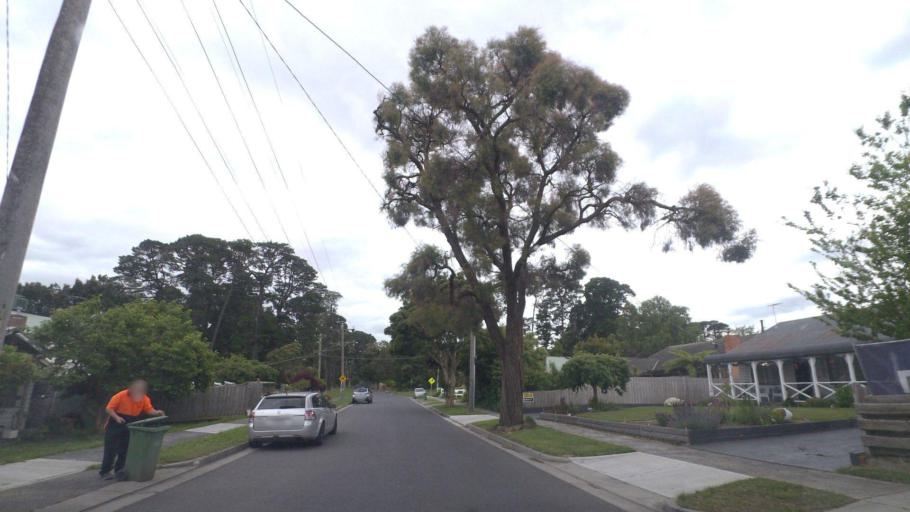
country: AU
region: Victoria
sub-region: Yarra Ranges
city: Mount Evelyn
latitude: -37.7865
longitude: 145.3725
